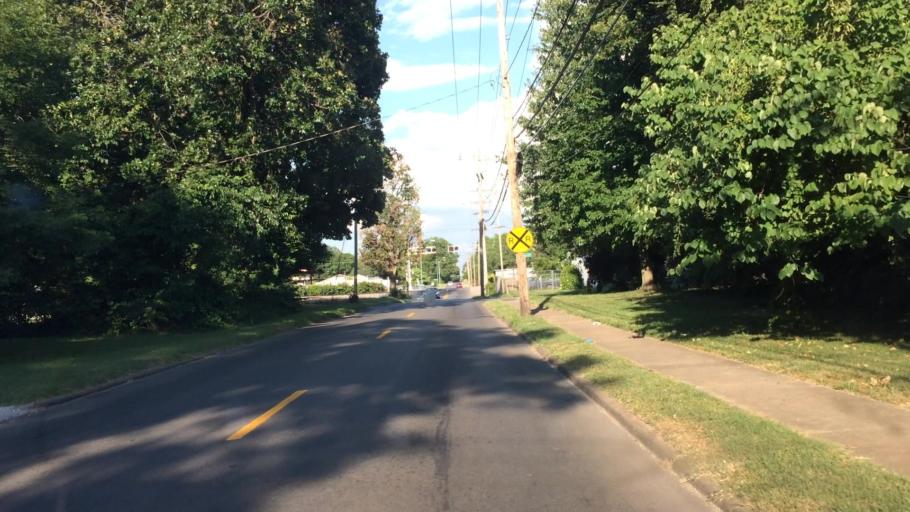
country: US
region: Missouri
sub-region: Greene County
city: Springfield
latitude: 37.1962
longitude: -93.2600
